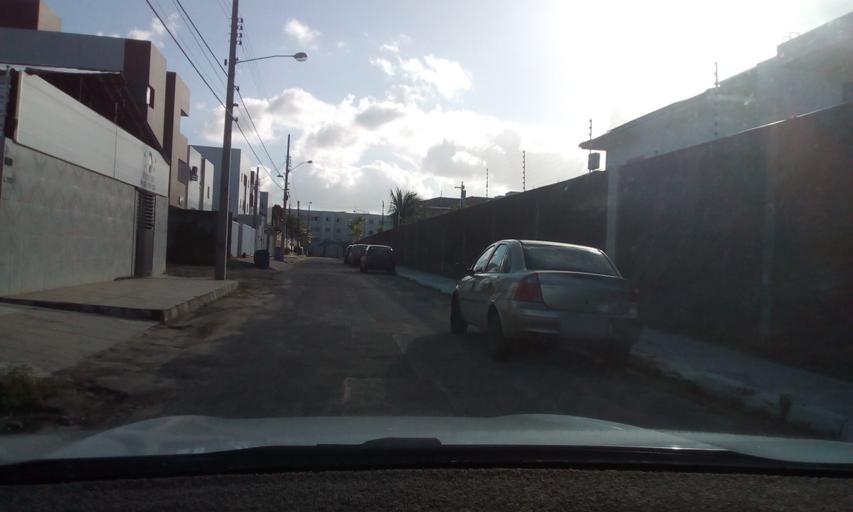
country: BR
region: Paraiba
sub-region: Joao Pessoa
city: Joao Pessoa
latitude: -7.1571
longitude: -34.8204
